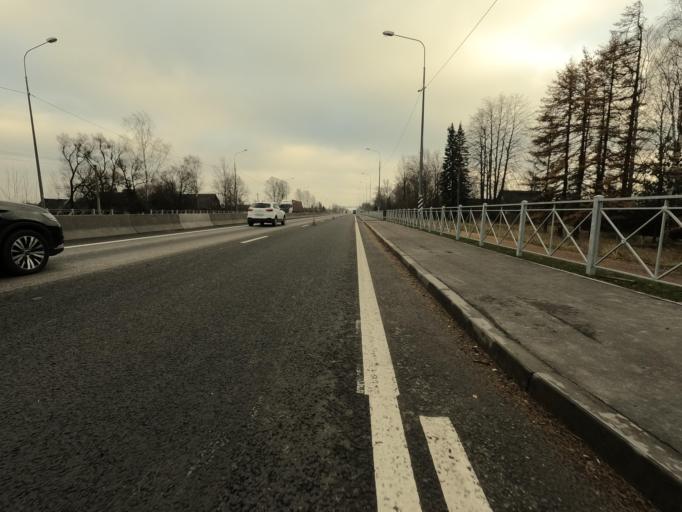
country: RU
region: Leningrad
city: Mga
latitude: 59.7202
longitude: 31.1031
